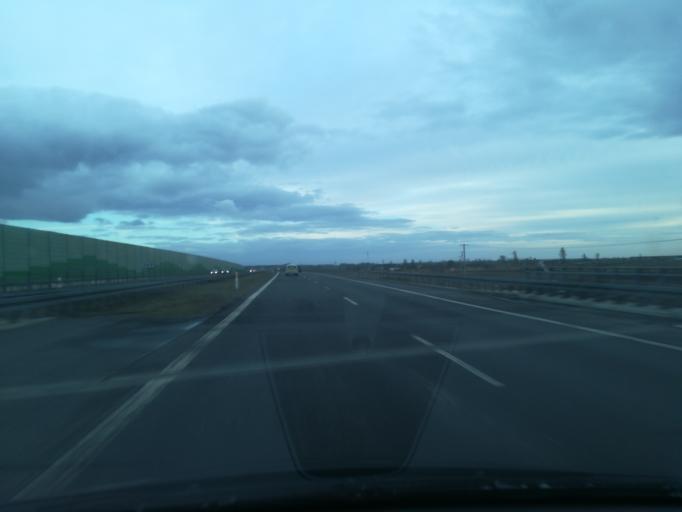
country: PL
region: Lodz Voivodeship
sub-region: Powiat leczycki
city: Piatek
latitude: 52.0956
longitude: 19.5167
